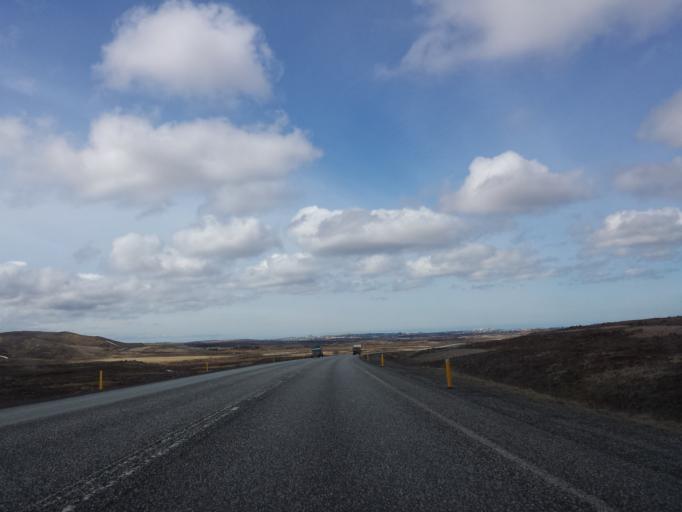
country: IS
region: Capital Region
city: Mosfellsbaer
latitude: 64.0720
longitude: -21.6276
